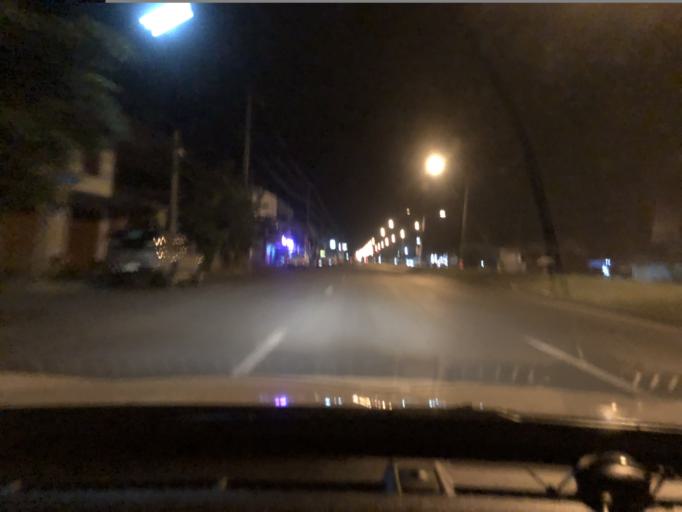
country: TH
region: Nakhon Sawan
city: Takhli
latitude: 15.2639
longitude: 100.3378
